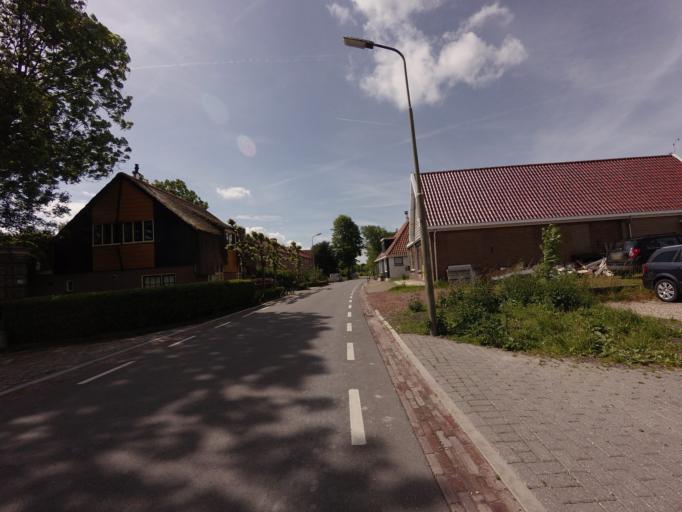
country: NL
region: North Holland
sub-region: Gemeente Opmeer
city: Opmeer
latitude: 52.6623
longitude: 4.9752
